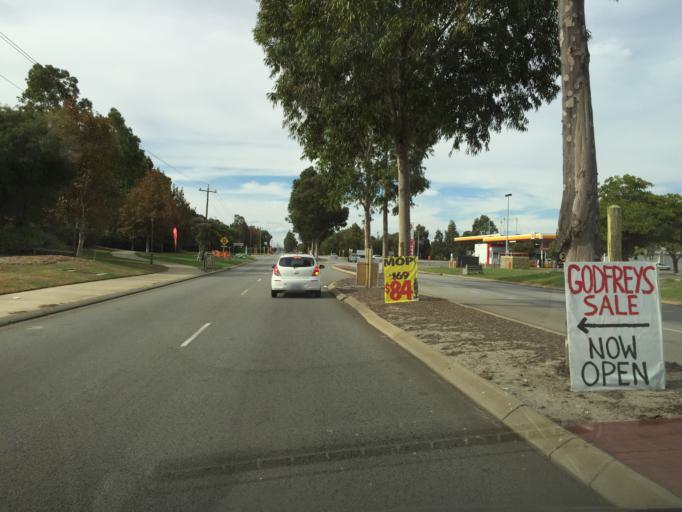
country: AU
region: Western Australia
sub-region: Canning
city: Willetton
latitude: -32.0709
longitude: 115.8943
